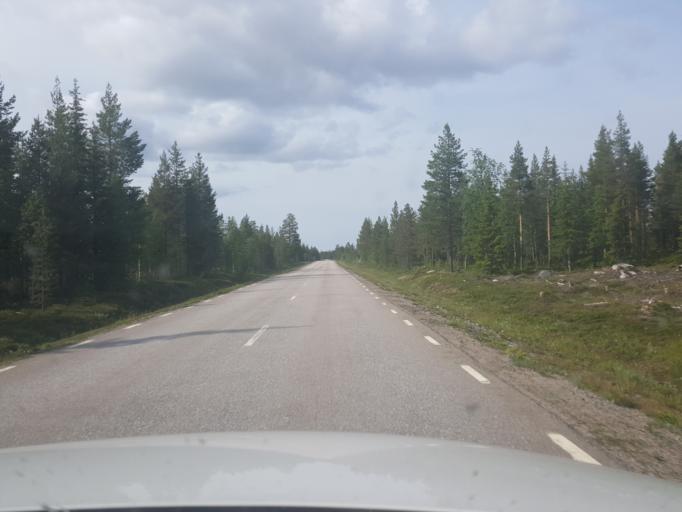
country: SE
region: Norrbotten
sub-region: Arjeplogs Kommun
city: Arjeplog
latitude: 65.6693
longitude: 18.0784
